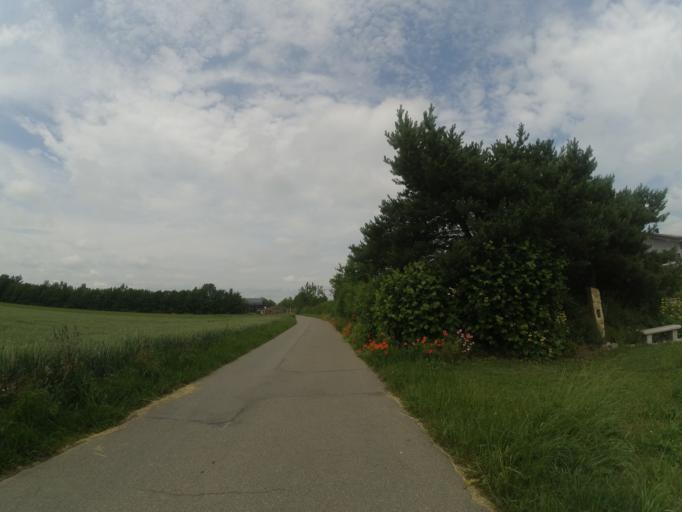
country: DE
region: Baden-Wuerttemberg
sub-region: Tuebingen Region
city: Leutkirch im Allgau
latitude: 47.8155
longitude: 10.0204
